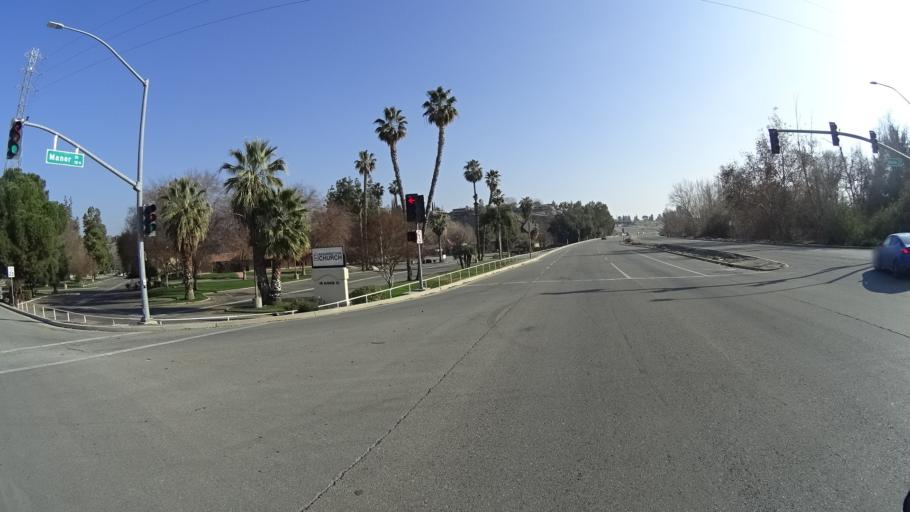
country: US
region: California
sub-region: Kern County
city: Oildale
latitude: 35.4046
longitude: -119.0071
